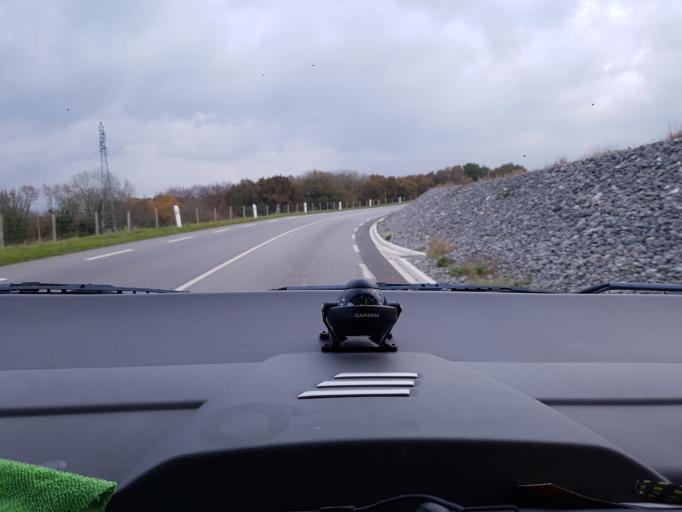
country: FR
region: Haute-Normandie
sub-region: Departement de la Seine-Maritime
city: Hautot-sur-Mer
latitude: 49.8954
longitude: 1.0522
